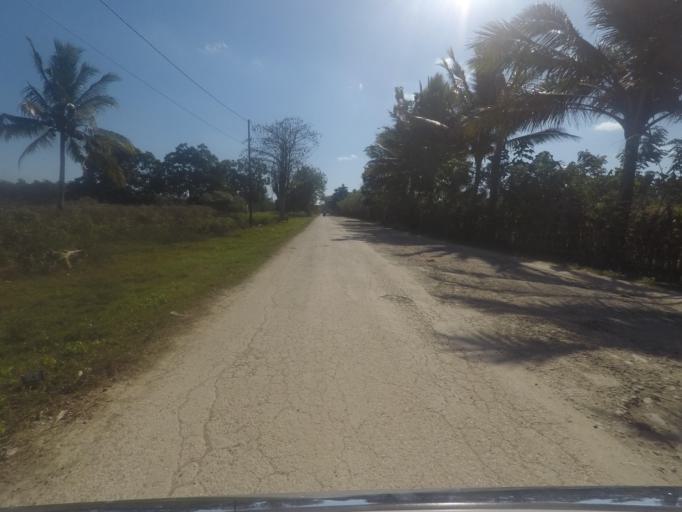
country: TL
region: Lautem
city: Lospalos
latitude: -8.5088
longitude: 126.9955
